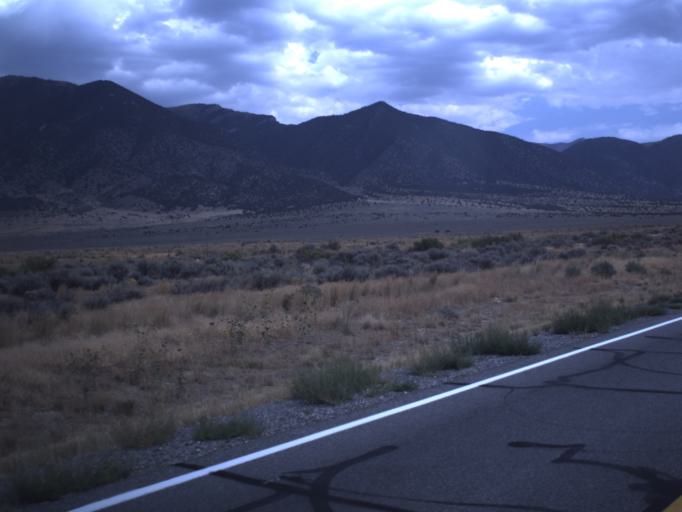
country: US
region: Utah
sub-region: Tooele County
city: Tooele
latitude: 40.3650
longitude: -112.3410
